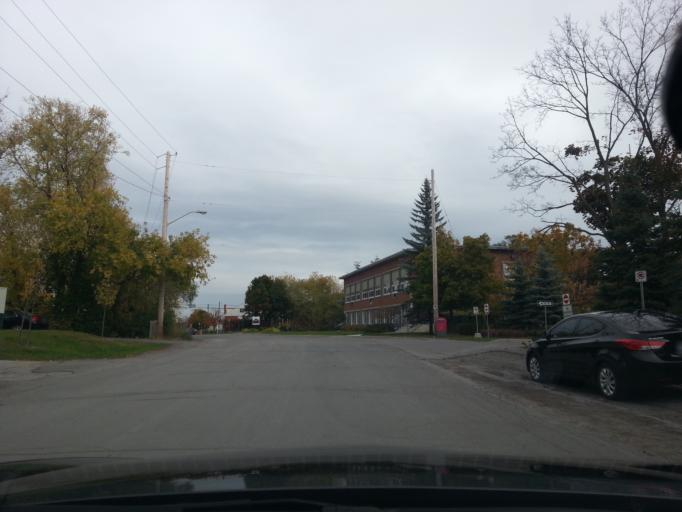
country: CA
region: Ontario
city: Ottawa
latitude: 45.3765
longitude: -75.7532
